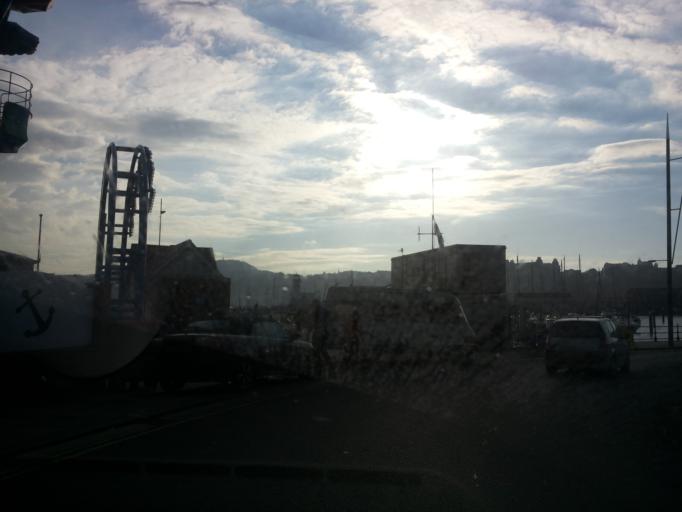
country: GB
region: England
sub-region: North Yorkshire
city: Scarborough
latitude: 54.2841
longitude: -0.3868
